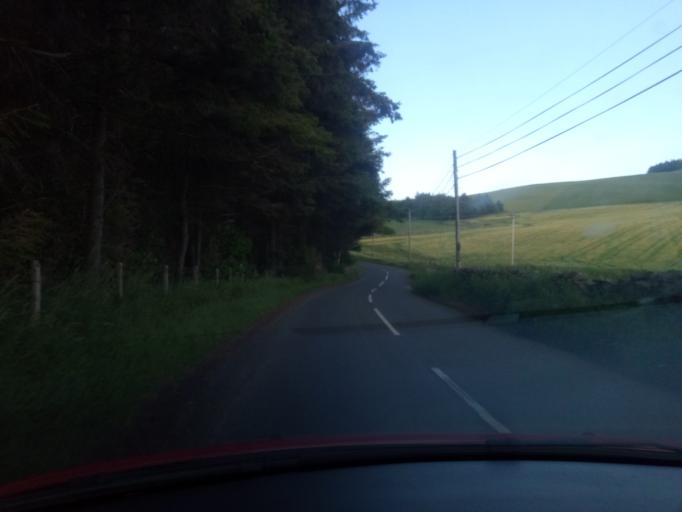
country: GB
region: Scotland
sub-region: The Scottish Borders
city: Selkirk
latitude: 55.5139
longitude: -2.9305
